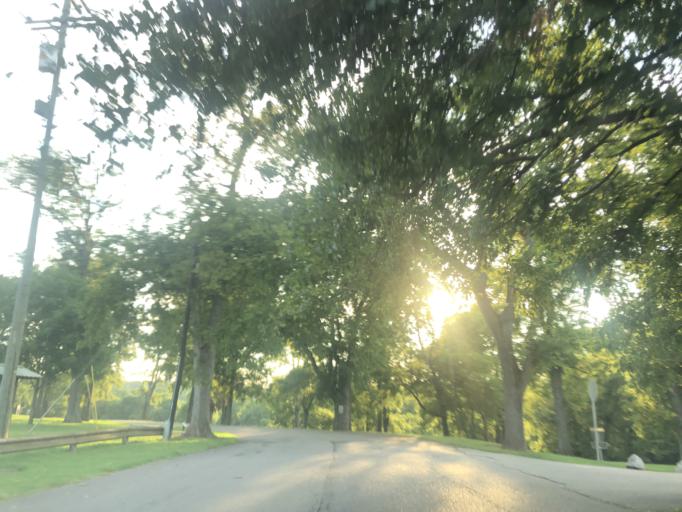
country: US
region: Tennessee
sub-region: Davidson County
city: Nashville
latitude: 36.1662
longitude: -86.7405
